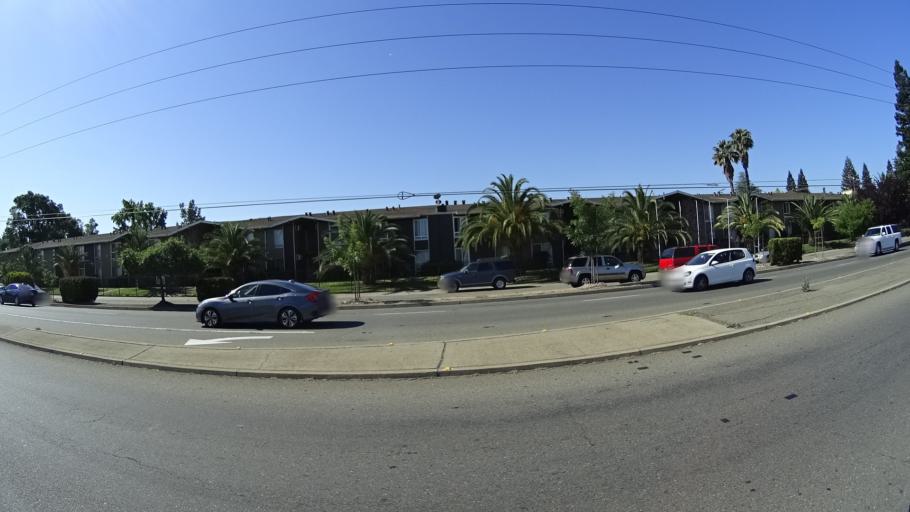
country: US
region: California
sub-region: Sacramento County
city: Parkway
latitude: 38.4957
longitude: -121.5100
